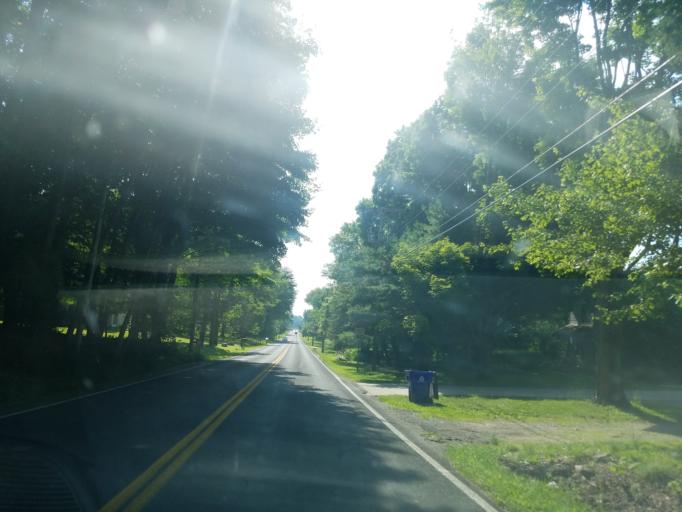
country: US
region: Ohio
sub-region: Summit County
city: Mogadore
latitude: 41.0509
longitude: -81.3757
